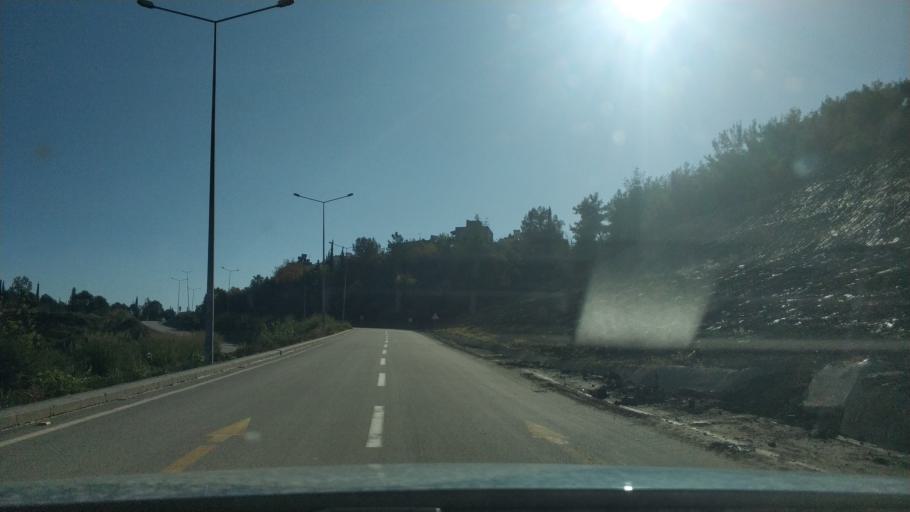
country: TR
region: Adana
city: Seyhan
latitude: 37.0645
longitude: 35.2696
